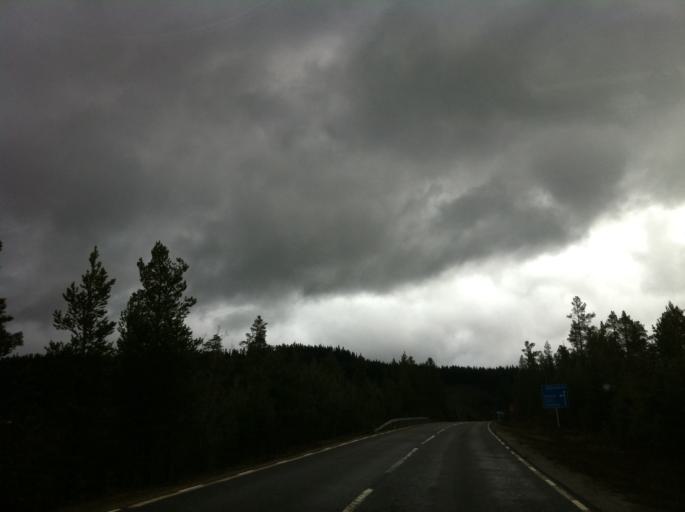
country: NO
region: Hedmark
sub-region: Engerdal
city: Engerdal
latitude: 62.4246
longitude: 12.7364
